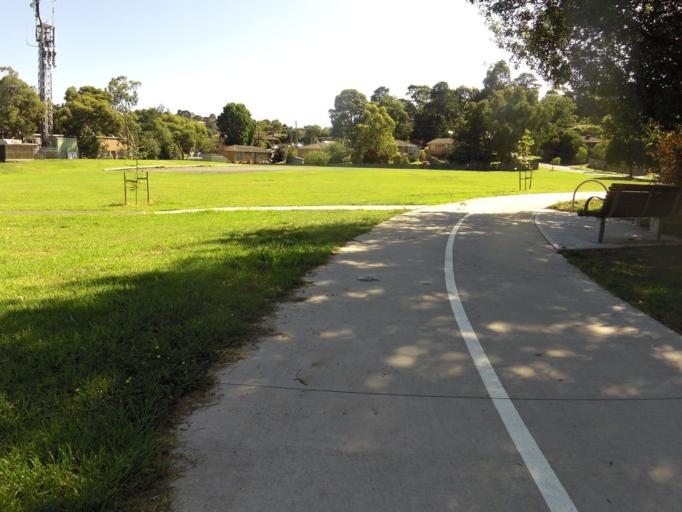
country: AU
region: Victoria
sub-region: Yarra Ranges
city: Kilsyth
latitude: -37.7865
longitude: 145.3205
